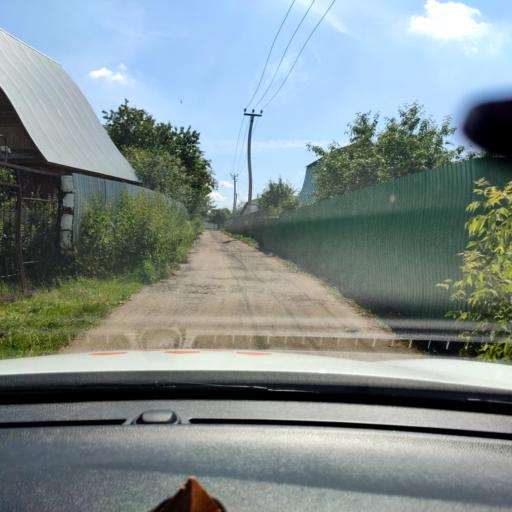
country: RU
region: Tatarstan
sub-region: Gorod Kazan'
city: Kazan
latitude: 55.8339
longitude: 49.2224
